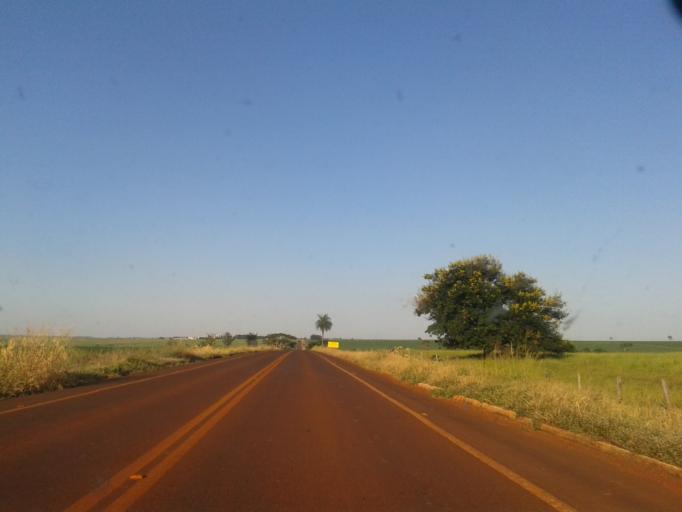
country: BR
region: Minas Gerais
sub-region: Capinopolis
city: Capinopolis
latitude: -18.7093
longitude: -49.7121
